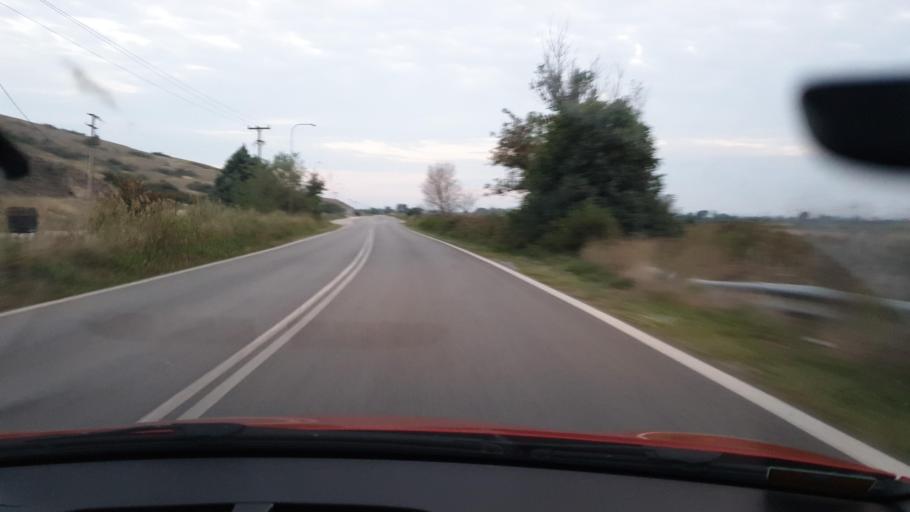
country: GR
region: Central Macedonia
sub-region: Nomos Kilkis
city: Polykastro
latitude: 41.0098
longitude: 22.6365
